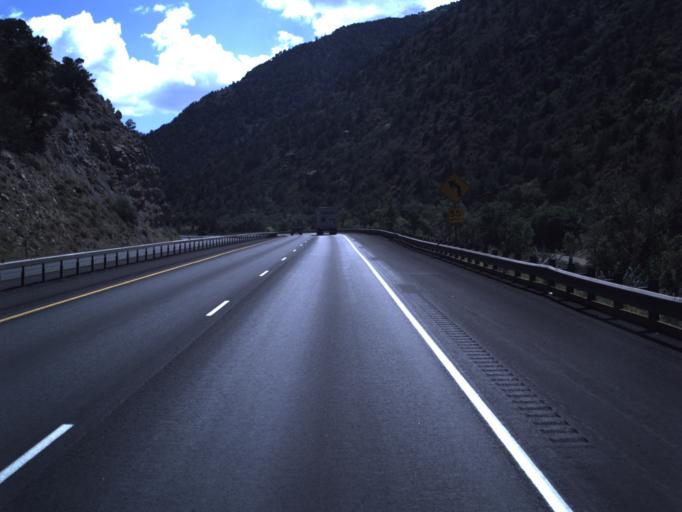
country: US
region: Utah
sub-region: Sevier County
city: Salina
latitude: 38.8975
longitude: -111.6301
